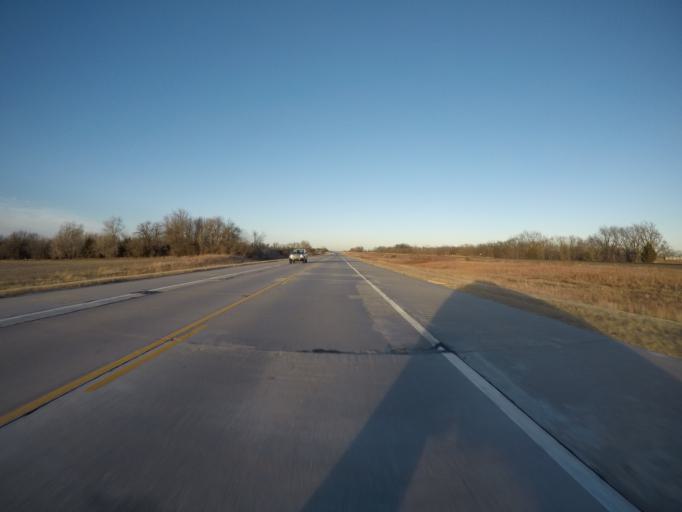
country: US
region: Kansas
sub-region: Harvey County
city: North Newton
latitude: 38.0760
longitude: -97.2984
